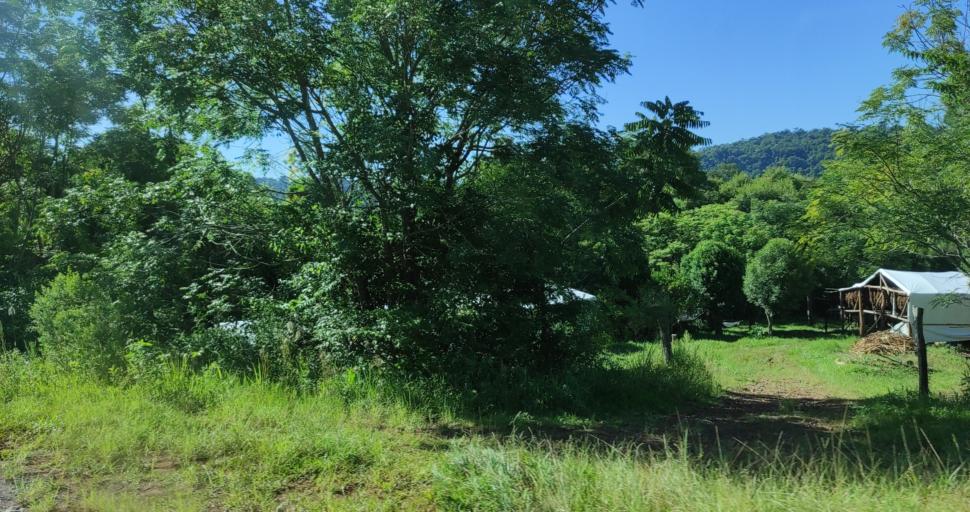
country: AR
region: Misiones
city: El Soberbio
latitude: -27.2475
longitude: -54.0326
